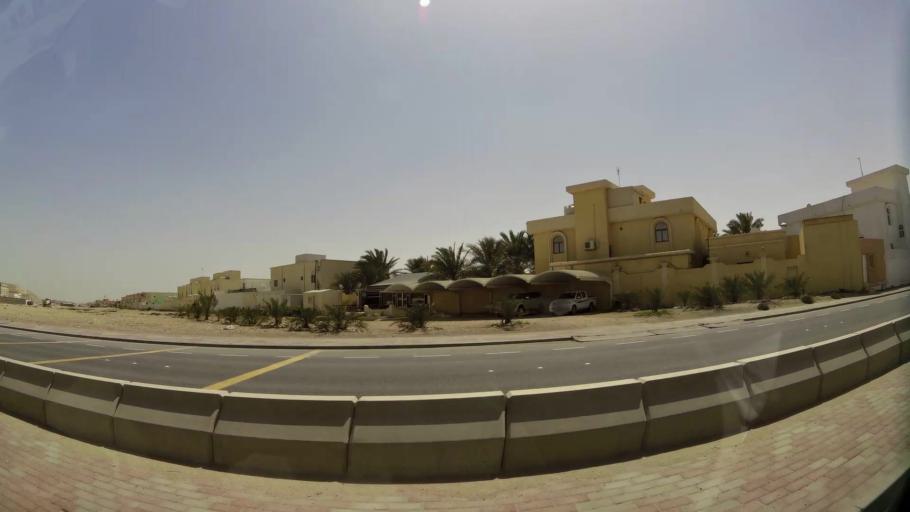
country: QA
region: Baladiyat Umm Salal
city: Umm Salal Muhammad
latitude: 25.3636
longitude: 51.4399
